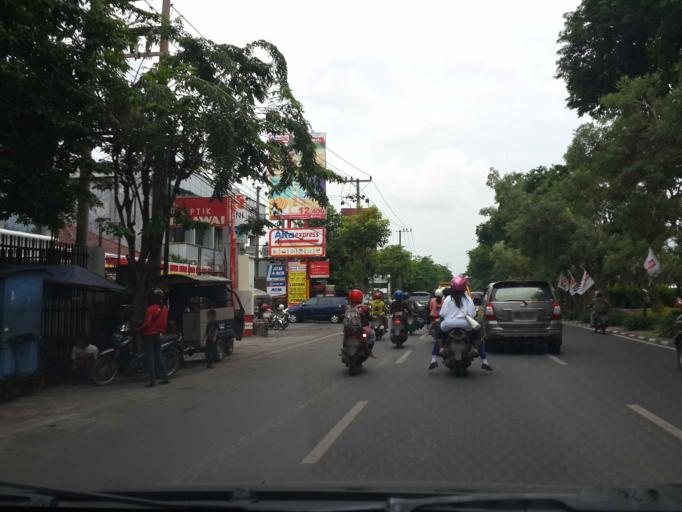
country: ID
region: East Java
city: Gubengairlangga
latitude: -7.2786
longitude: 112.7297
